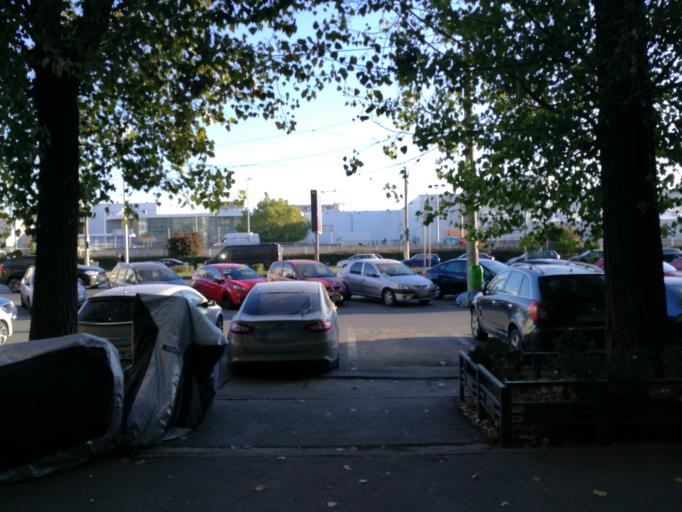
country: RO
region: Ilfov
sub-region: Comuna Chiajna
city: Rosu
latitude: 44.4352
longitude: 26.0375
